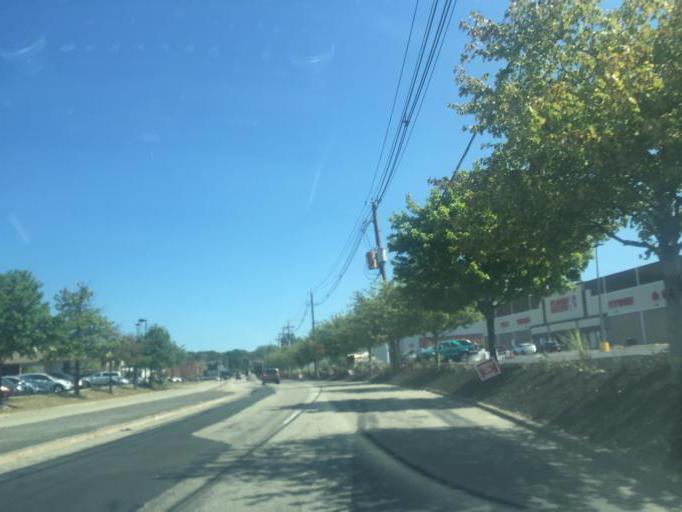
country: US
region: New Jersey
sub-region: Passaic County
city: Singac
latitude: 40.8874
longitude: -74.2537
